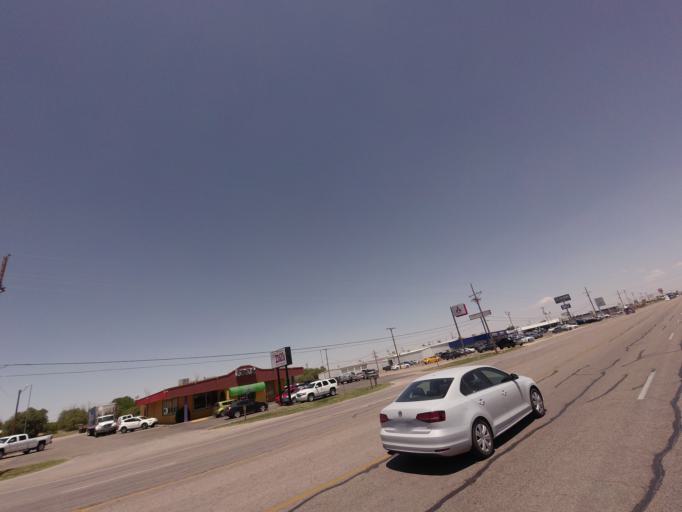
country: US
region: New Mexico
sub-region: Curry County
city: Clovis
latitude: 34.3953
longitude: -103.1638
